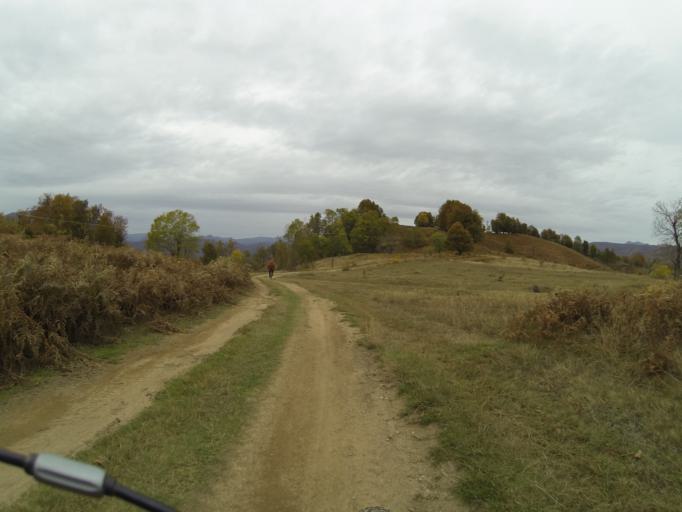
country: RO
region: Gorj
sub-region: Comuna Pades
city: Closani
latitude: 45.1136
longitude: 22.8493
